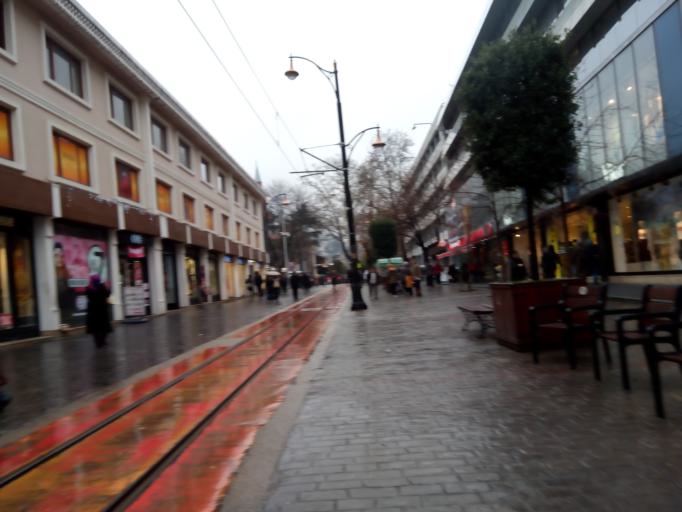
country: TR
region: Bursa
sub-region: Osmangazi
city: Bursa
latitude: 40.1858
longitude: 29.0643
